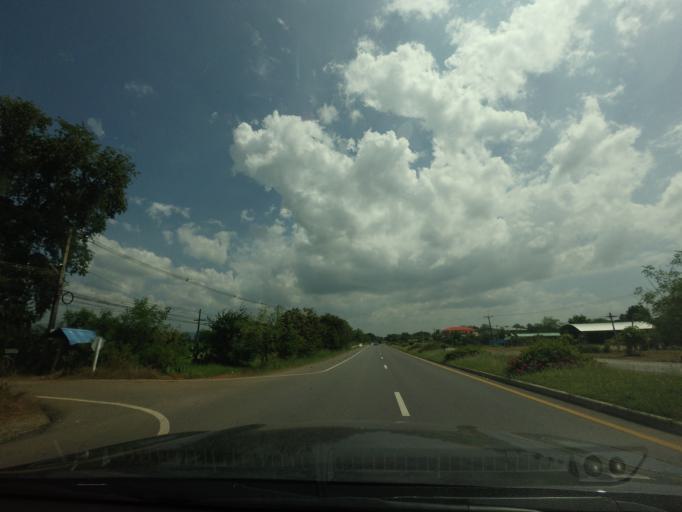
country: TH
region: Phetchabun
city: Phetchabun
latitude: 16.2311
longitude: 101.0845
